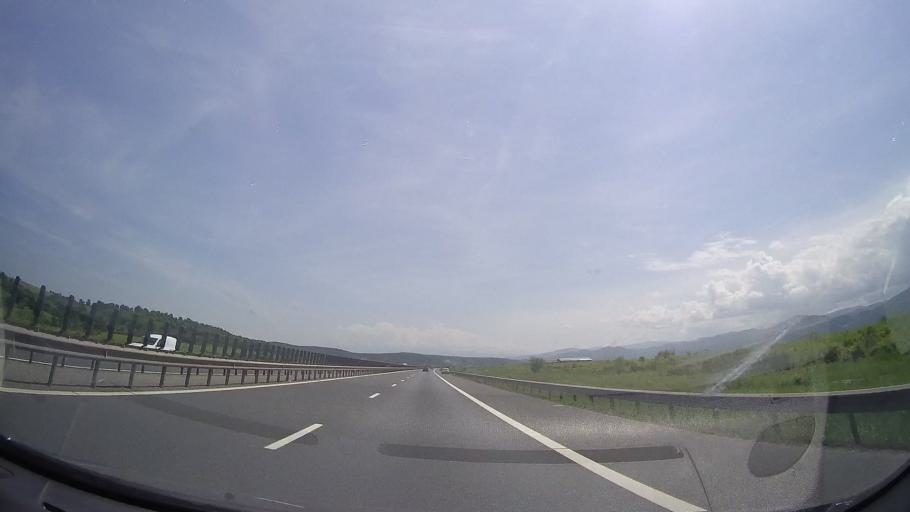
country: RO
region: Sibiu
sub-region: Oras Saliste
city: Saliste
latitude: 45.8055
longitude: 23.9127
